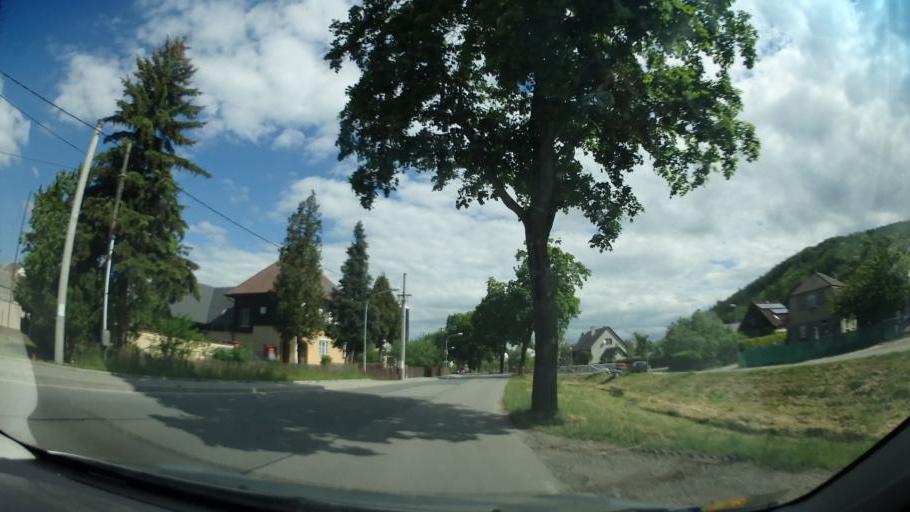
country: CZ
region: Pardubicky
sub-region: Okres Svitavy
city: Moravska Trebova
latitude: 49.7735
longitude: 16.6628
